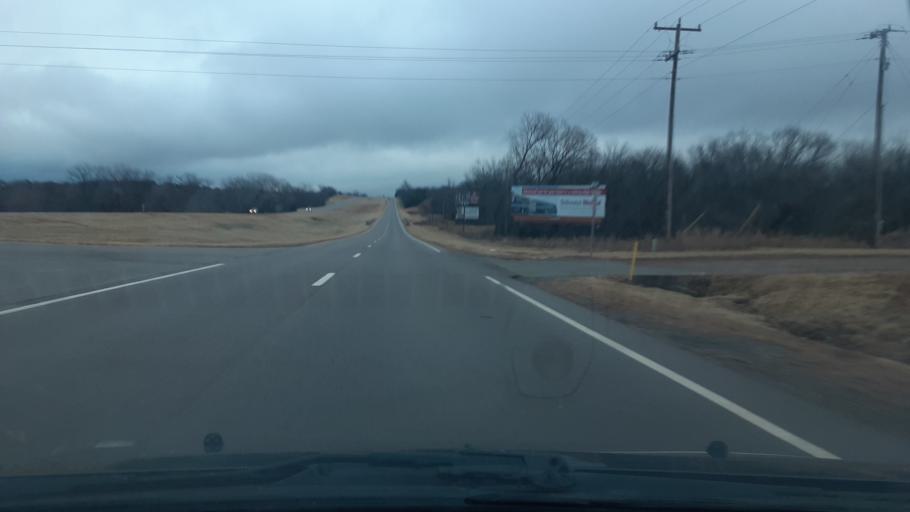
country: US
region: Oklahoma
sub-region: Payne County
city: Stillwater
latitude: 36.1158
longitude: -97.1587
